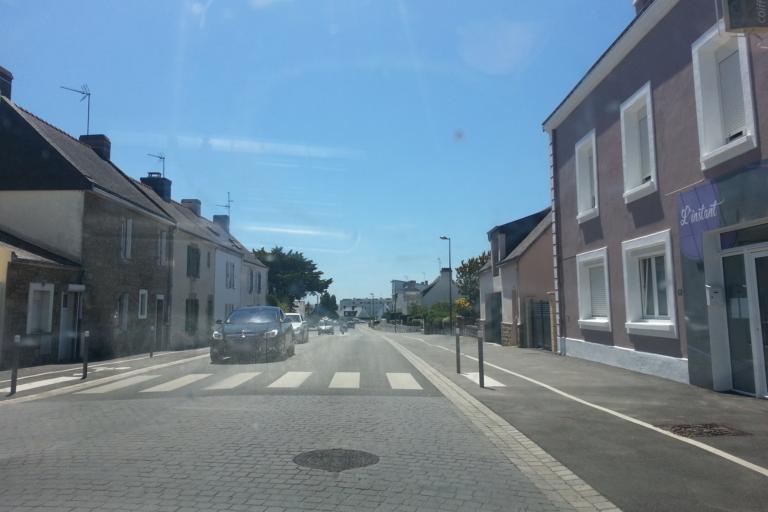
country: FR
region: Brittany
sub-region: Departement du Morbihan
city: Locmiquelic
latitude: 47.7177
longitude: -3.3402
